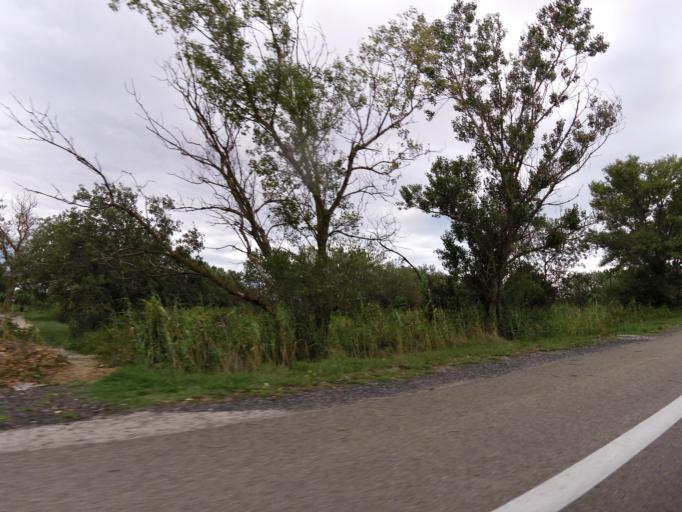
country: FR
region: Languedoc-Roussillon
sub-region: Departement du Gard
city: Aigues-Mortes
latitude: 43.5705
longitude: 4.1717
